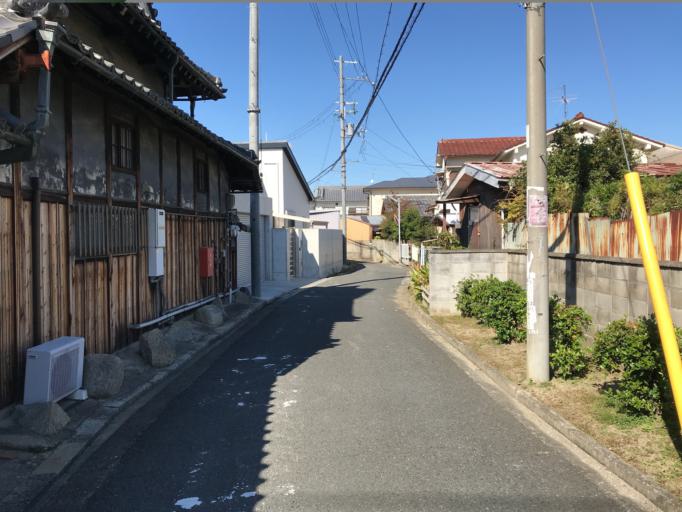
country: JP
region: Osaka
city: Tondabayashicho
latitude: 34.5341
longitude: 135.6117
